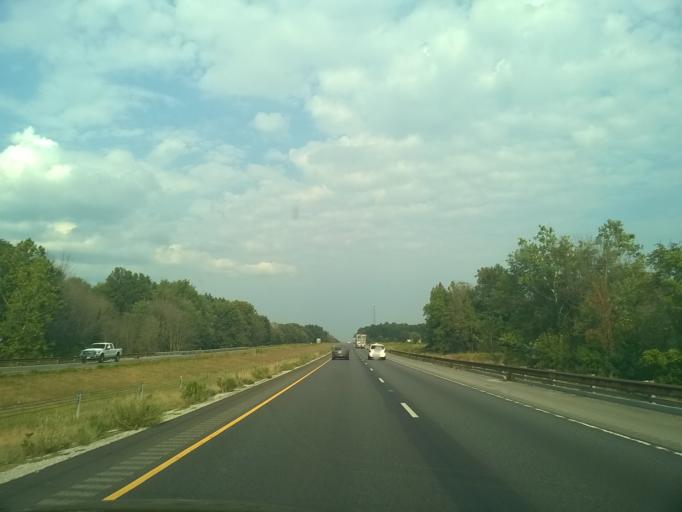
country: US
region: Indiana
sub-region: Clay County
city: Brazil
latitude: 39.4648
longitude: -87.0623
